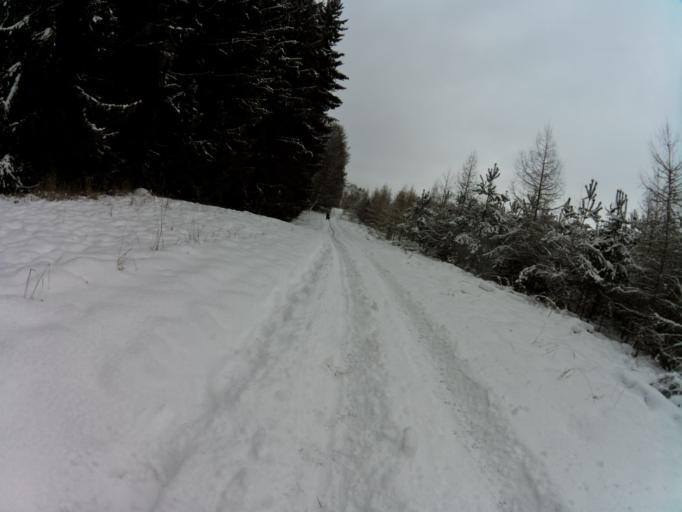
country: PL
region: West Pomeranian Voivodeship
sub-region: Powiat stargardzki
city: Dobrzany
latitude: 53.3543
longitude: 15.5096
